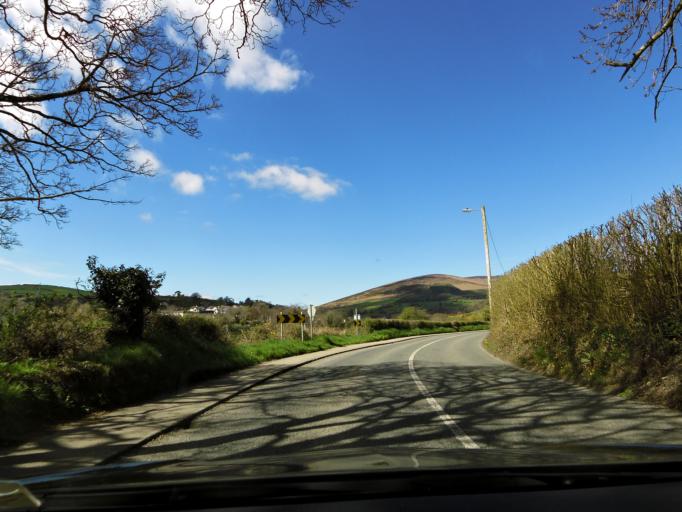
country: IE
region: Leinster
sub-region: Wicklow
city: Carnew
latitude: 52.7945
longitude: -6.4599
